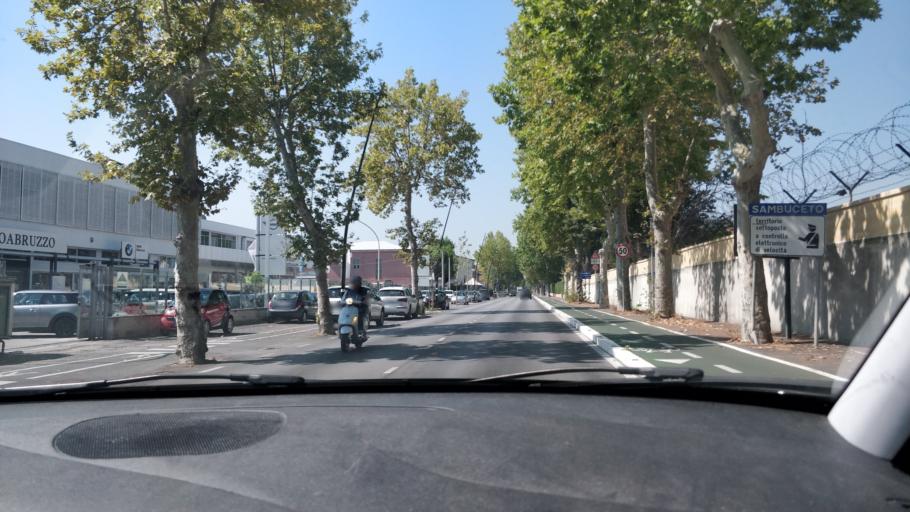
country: IT
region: Abruzzo
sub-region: Provincia di Chieti
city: Sambuceto
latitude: 42.4364
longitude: 14.1938
